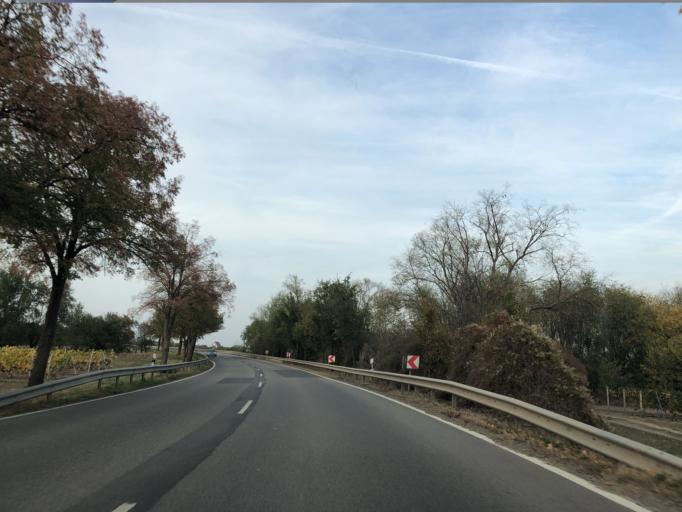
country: DE
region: Rheinland-Pfalz
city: Guntersblum
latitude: 49.7815
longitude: 8.3544
